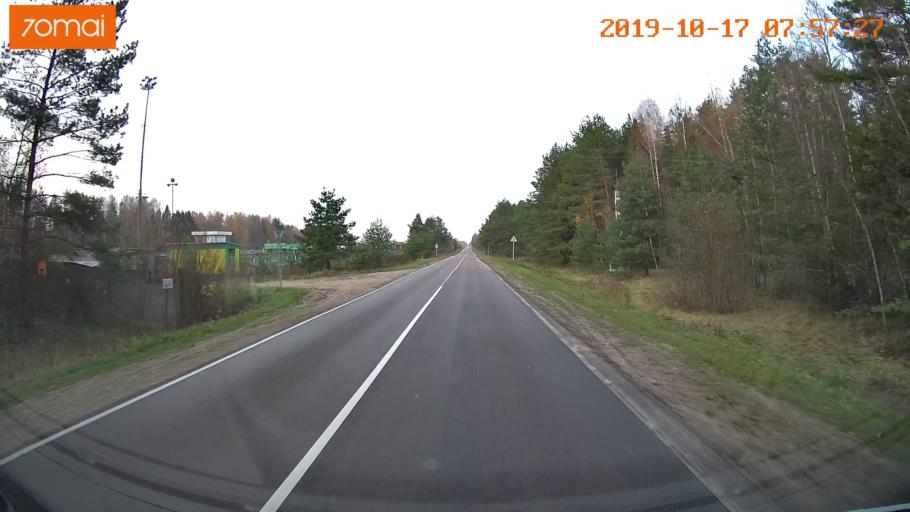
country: RU
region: Vladimir
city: Bavleny
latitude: 56.4116
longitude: 39.5759
